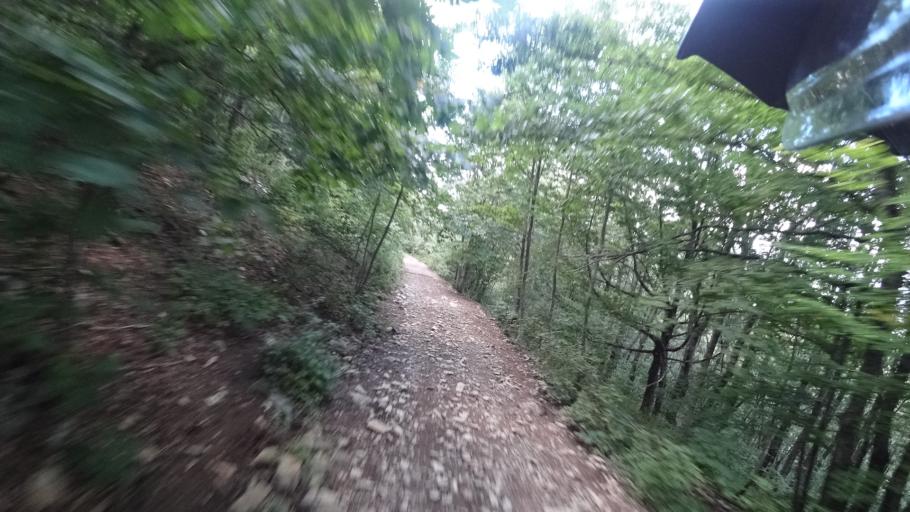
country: HR
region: Zadarska
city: Gracac
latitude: 44.3643
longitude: 16.0843
